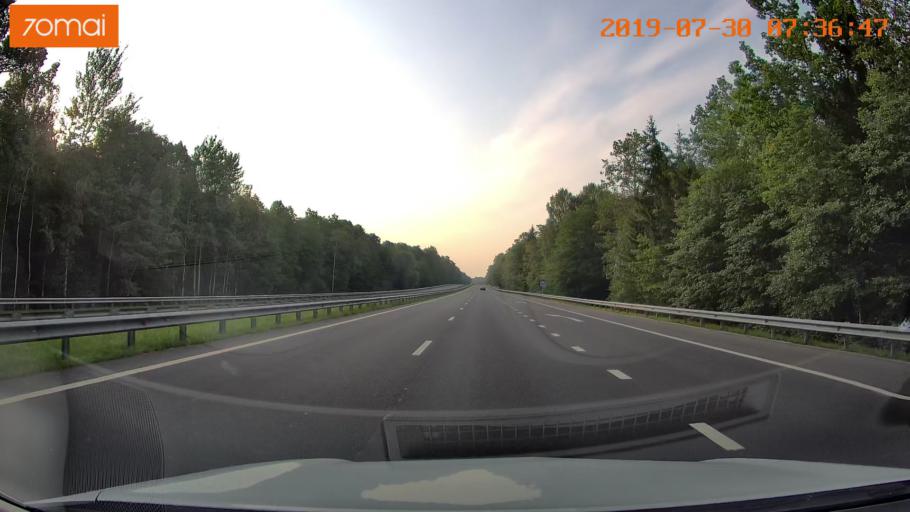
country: RU
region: Kaliningrad
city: Gvardeysk
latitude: 54.6614
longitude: 21.1322
